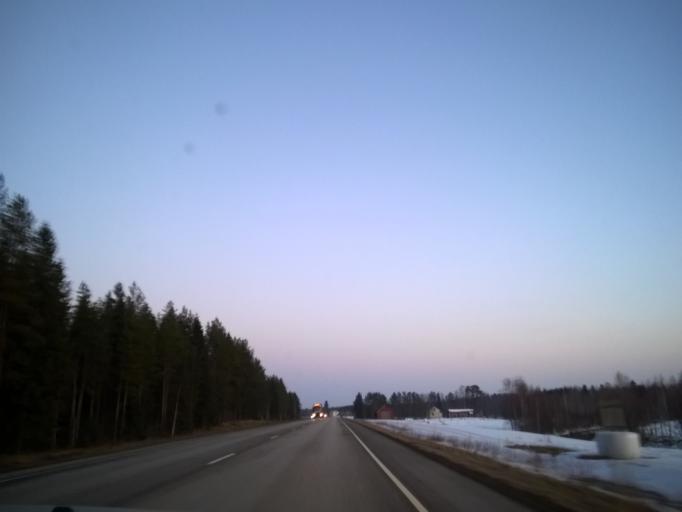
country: FI
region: Northern Ostrobothnia
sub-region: Nivala-Haapajaervi
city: Pyhaejaervi
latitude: 63.8182
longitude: 25.8948
